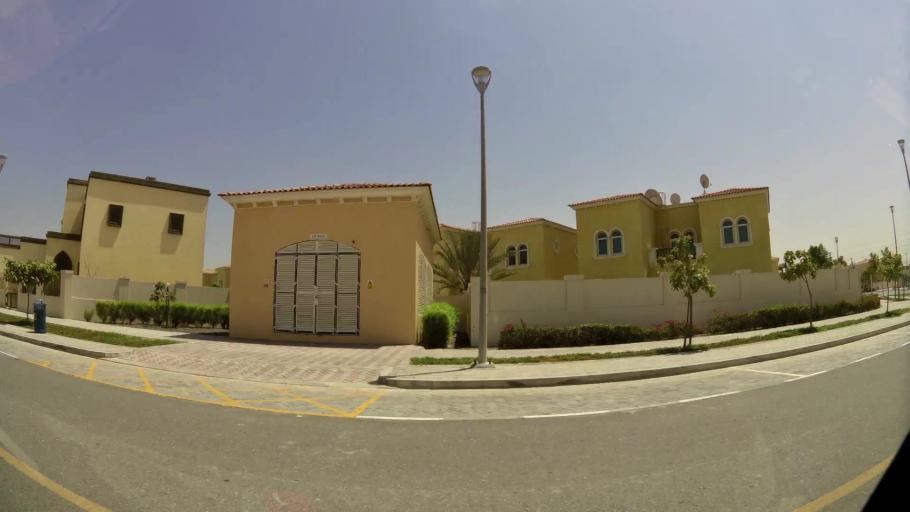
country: AE
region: Dubai
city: Dubai
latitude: 25.0344
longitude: 55.1653
